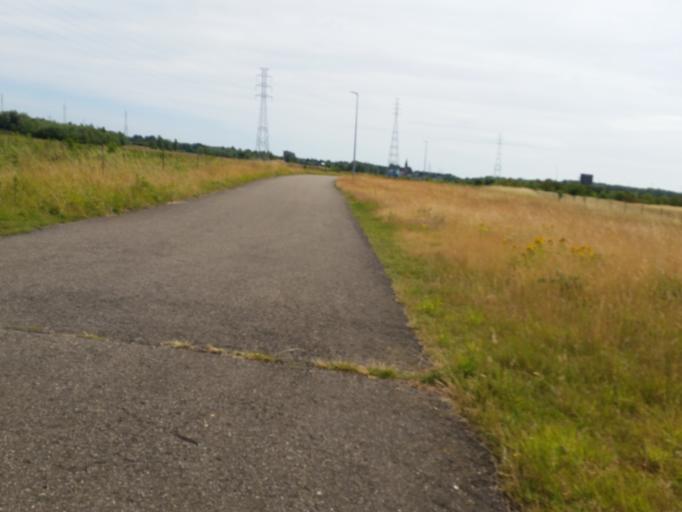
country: BE
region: Flanders
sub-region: Provincie Antwerpen
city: Niel
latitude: 51.1195
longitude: 4.3062
